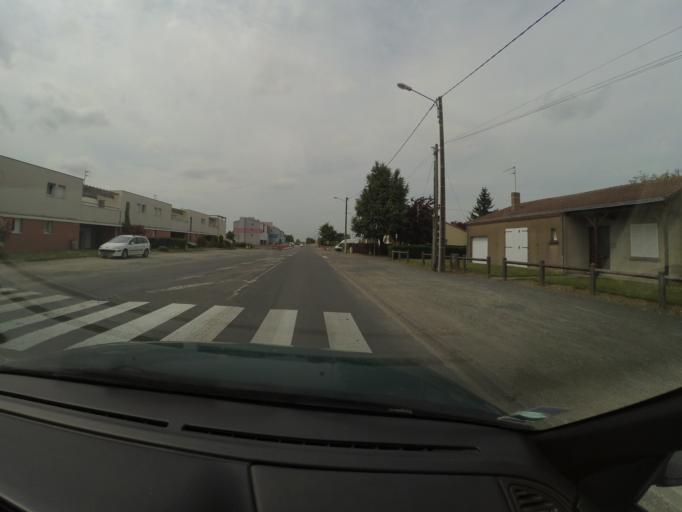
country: FR
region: Pays de la Loire
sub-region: Departement de la Loire-Atlantique
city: Gorges
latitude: 47.0951
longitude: -1.2919
